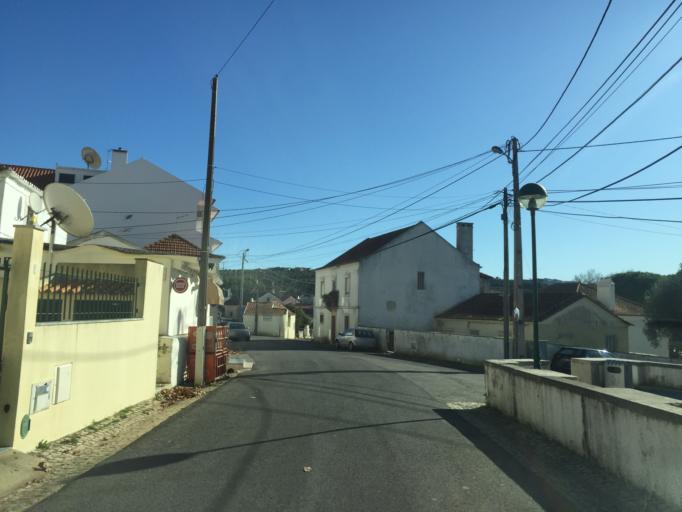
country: PT
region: Lisbon
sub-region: Sintra
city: Pero Pinheiro
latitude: 38.8555
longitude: -9.3216
